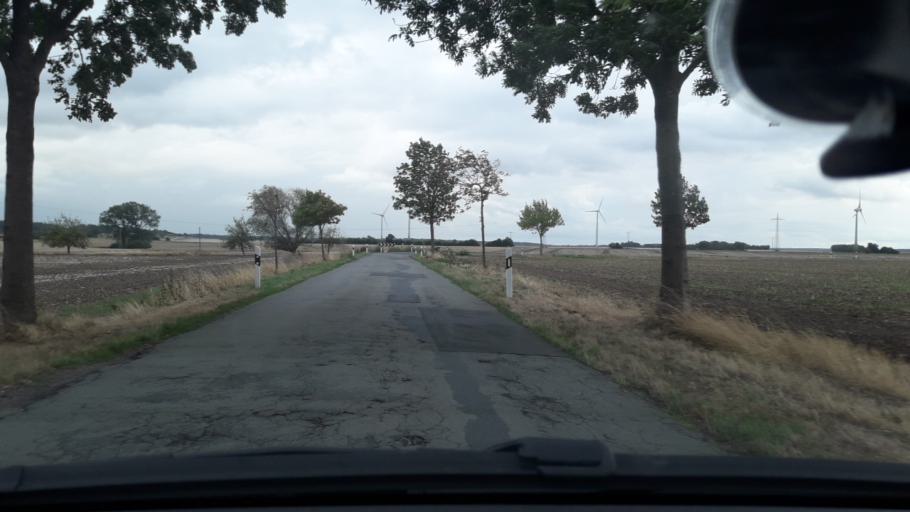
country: DE
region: Lower Saxony
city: Velpke
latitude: 52.3923
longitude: 10.9622
